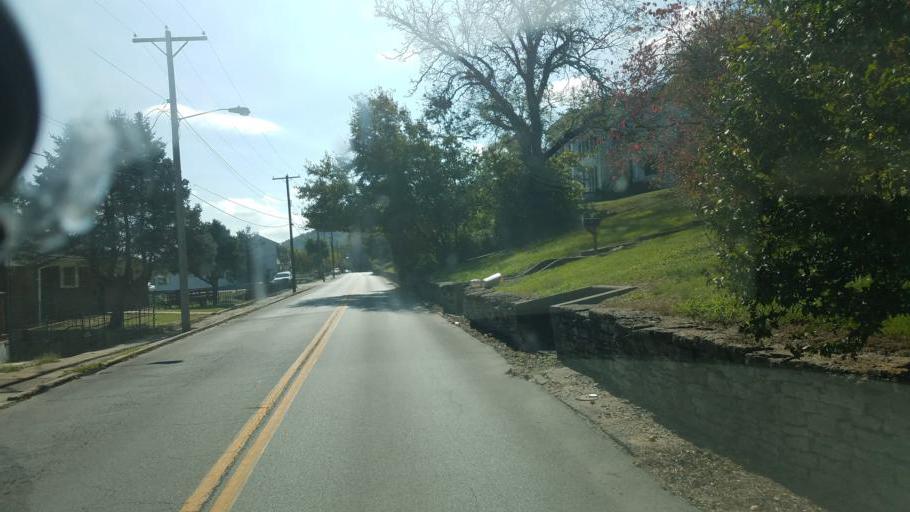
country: US
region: Ohio
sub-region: Brown County
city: Aberdeen
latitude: 38.6558
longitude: -83.7755
